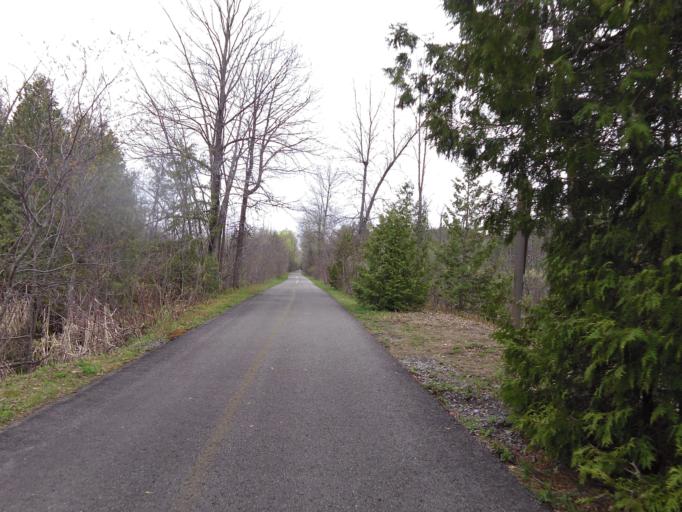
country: CA
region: Quebec
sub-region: Laurentides
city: Lachute
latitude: 45.5793
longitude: -74.3916
